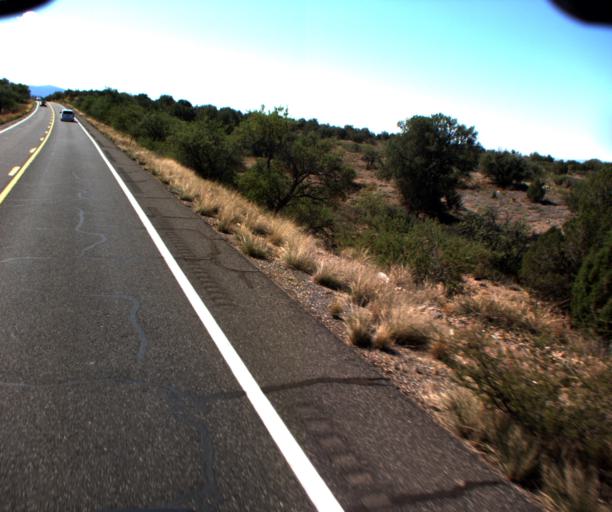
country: US
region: Arizona
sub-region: Yavapai County
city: Lake Montezuma
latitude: 34.7049
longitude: -111.7708
